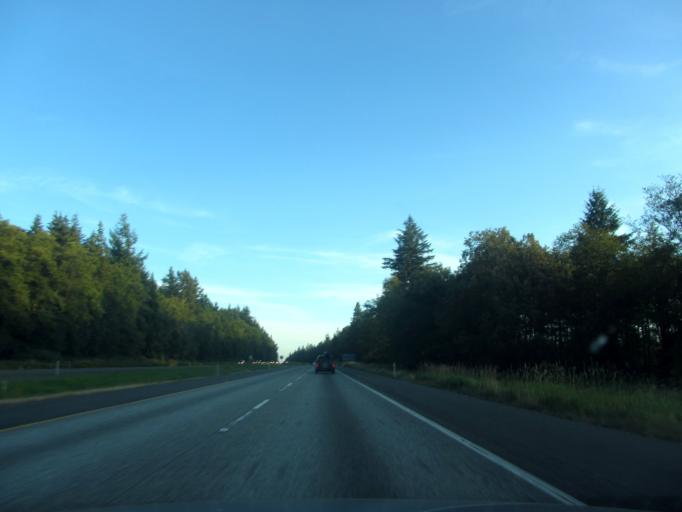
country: US
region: Washington
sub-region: Skagit County
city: Burlington
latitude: 48.5779
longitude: -122.3470
